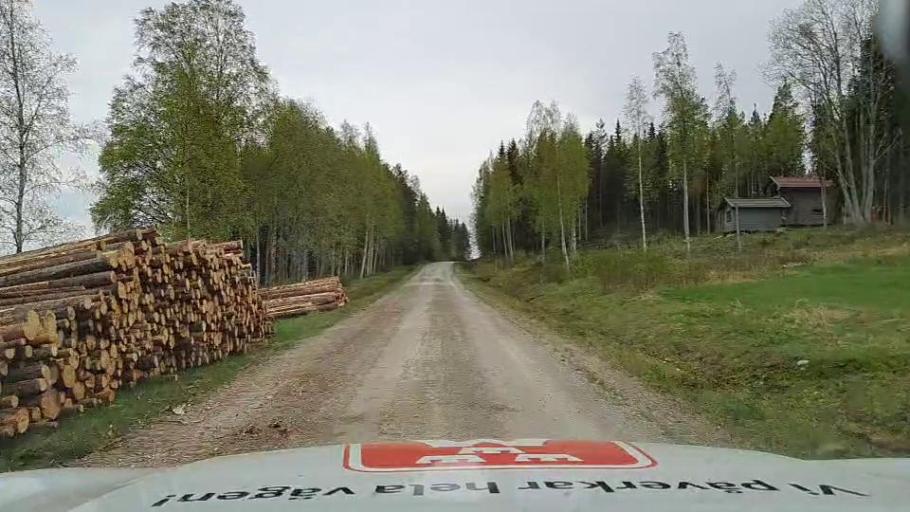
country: SE
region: Jaemtland
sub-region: Bergs Kommun
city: Hoverberg
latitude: 62.6862
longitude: 14.7745
